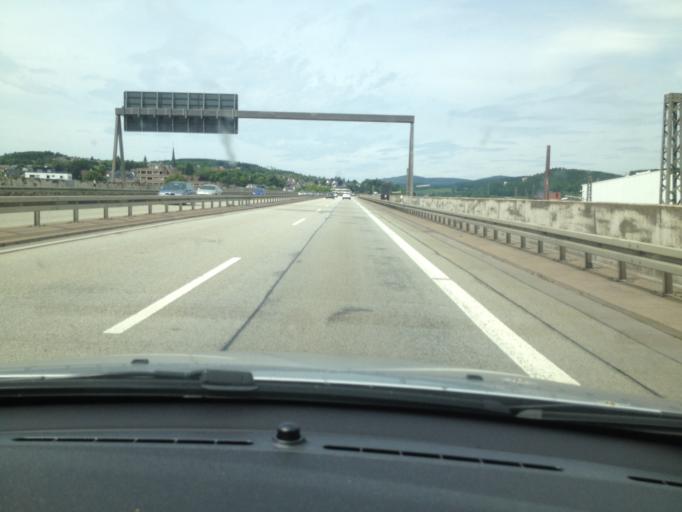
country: DE
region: North Rhine-Westphalia
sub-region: Regierungsbezirk Arnsberg
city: Siegen
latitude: 50.9101
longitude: 8.0140
